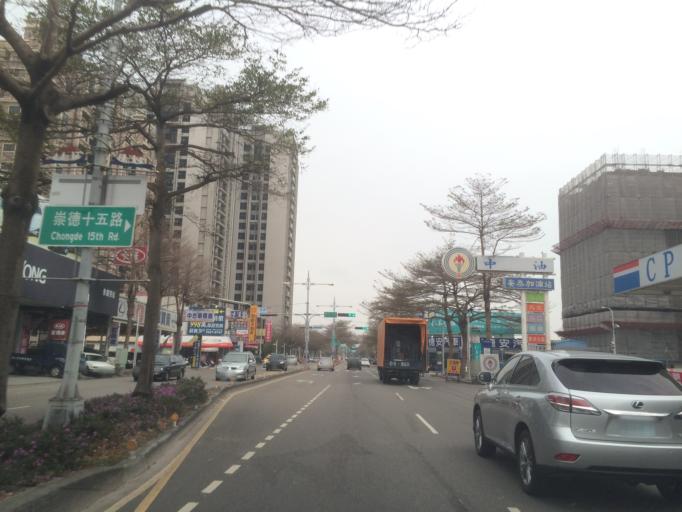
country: TW
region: Taiwan
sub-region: Taichung City
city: Taichung
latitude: 24.1945
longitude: 120.6865
